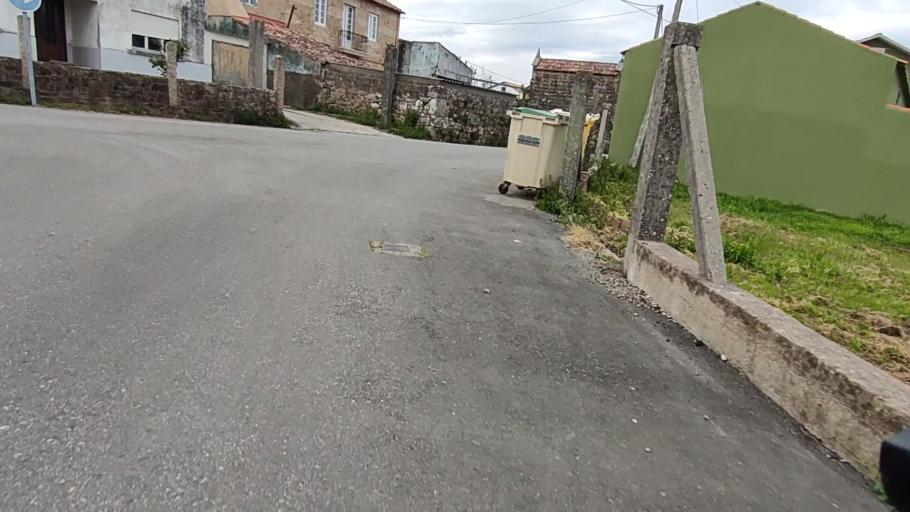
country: ES
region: Galicia
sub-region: Provincia da Coruna
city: Boiro
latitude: 42.6330
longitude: -8.8637
